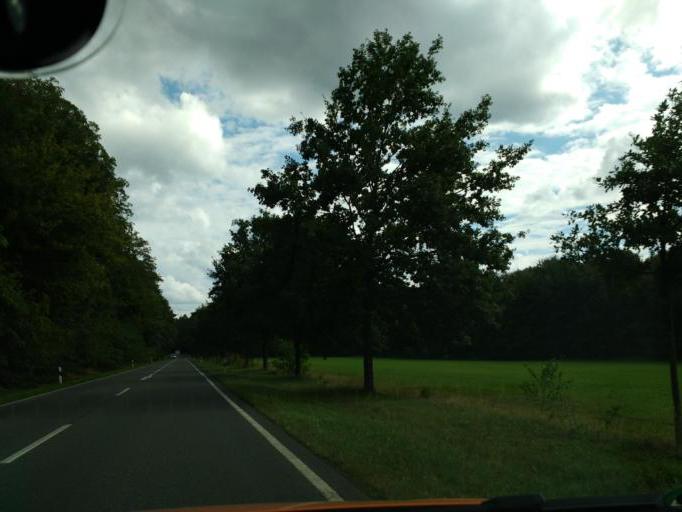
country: DE
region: Brandenburg
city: Marienwerder
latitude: 52.8515
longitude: 13.5802
